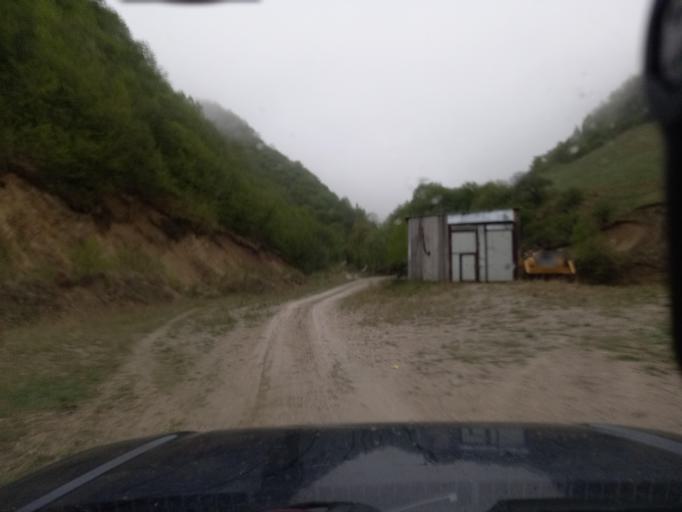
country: RU
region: Kabardino-Balkariya
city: Zhankhoteko
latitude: 43.4984
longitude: 43.1539
